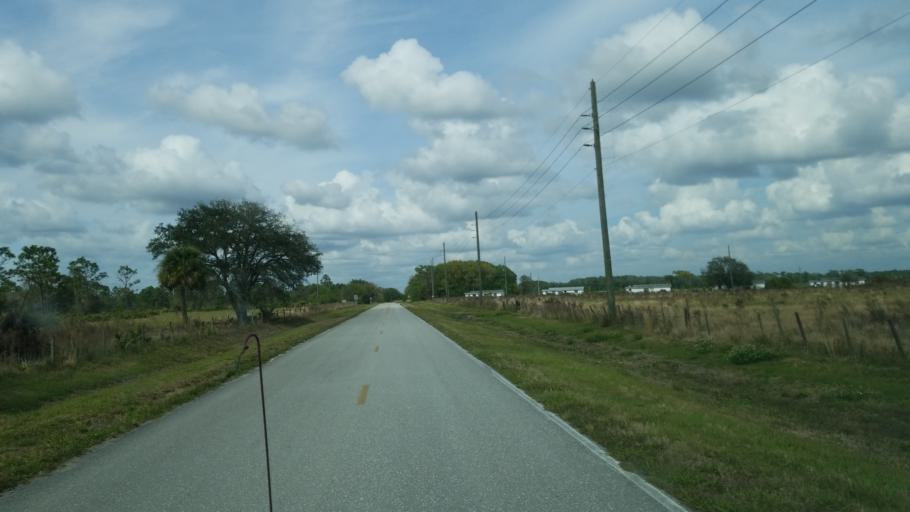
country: US
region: Florida
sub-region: Okeechobee County
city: Cypress Quarters
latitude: 27.5141
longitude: -80.7768
